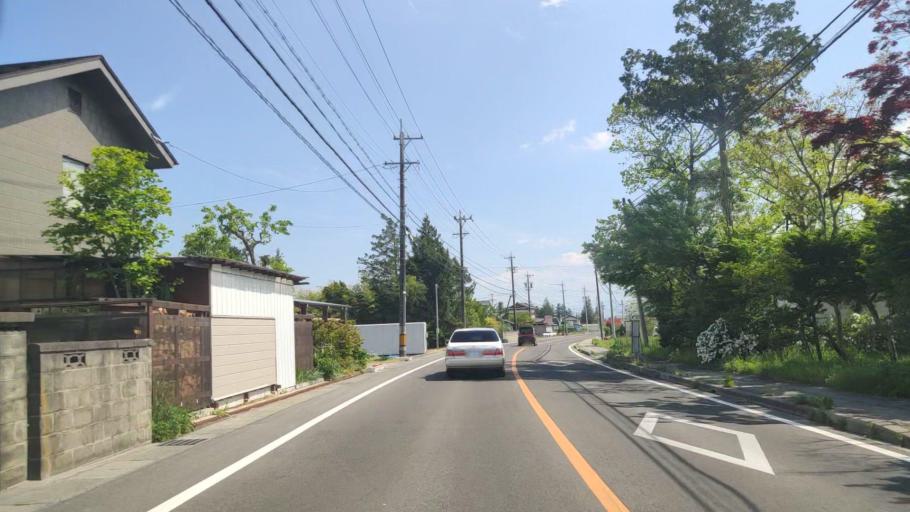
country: JP
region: Nagano
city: Hotaka
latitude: 36.4042
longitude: 137.8613
